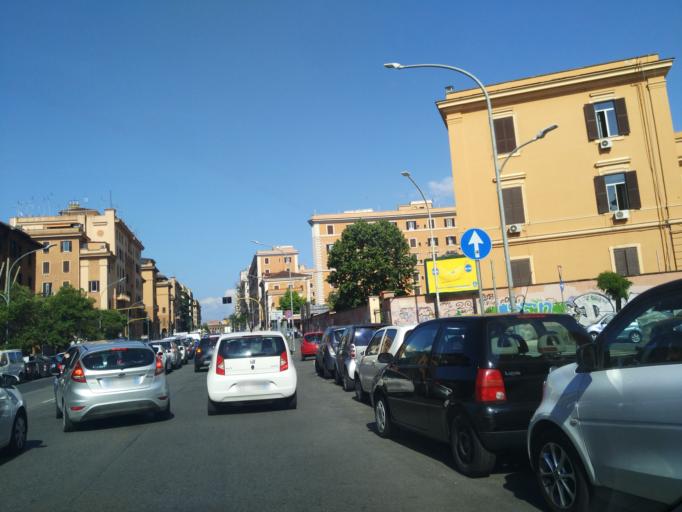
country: IT
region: Latium
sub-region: Citta metropolitana di Roma Capitale
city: Rome
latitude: 41.8860
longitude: 12.5141
